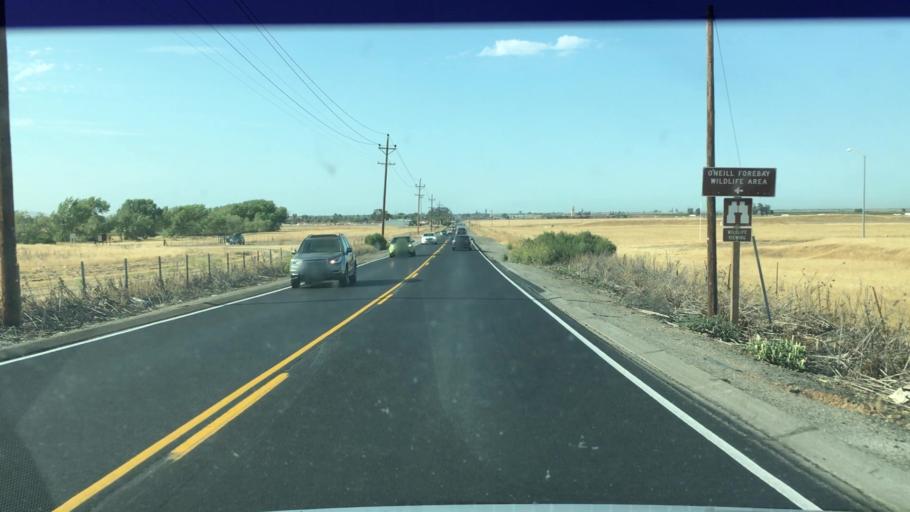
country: US
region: California
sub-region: Merced County
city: Los Banos
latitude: 37.0780
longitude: -121.0162
